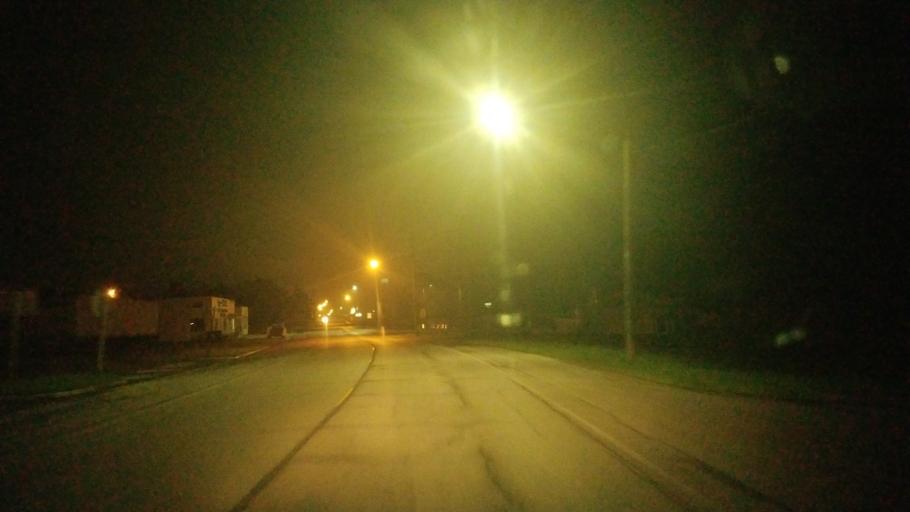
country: US
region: Missouri
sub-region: Pike County
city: Bowling Green
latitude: 39.3447
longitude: -91.2032
